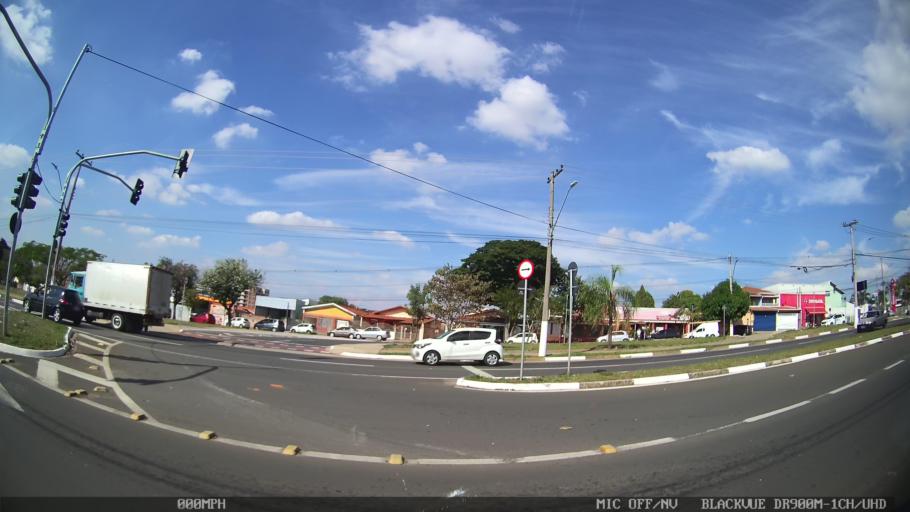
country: BR
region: Sao Paulo
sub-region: Hortolandia
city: Hortolandia
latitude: -22.8742
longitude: -47.2283
